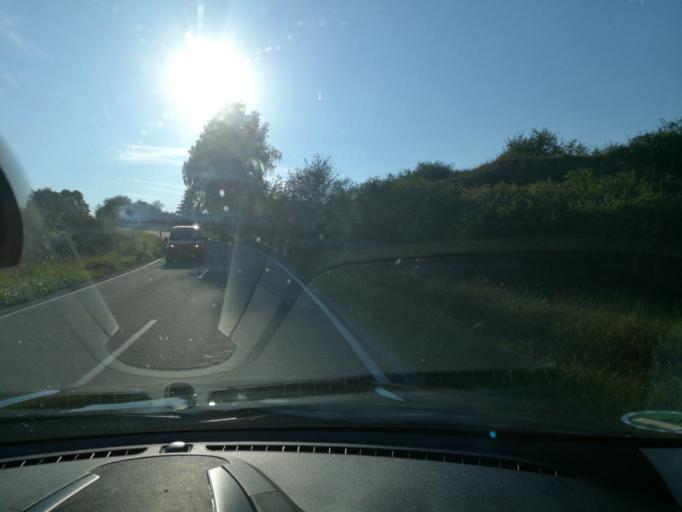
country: DE
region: Bavaria
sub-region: Upper Palatinate
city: Parsberg
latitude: 49.1752
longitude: 11.7005
